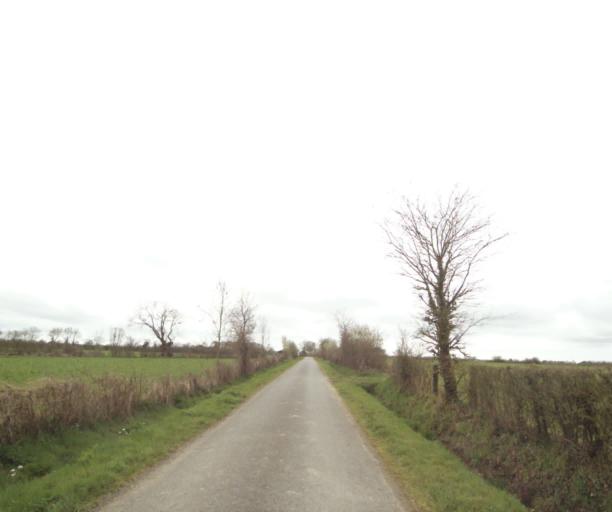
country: FR
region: Pays de la Loire
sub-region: Departement de la Loire-Atlantique
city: Bouvron
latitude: 47.4324
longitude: -1.8736
